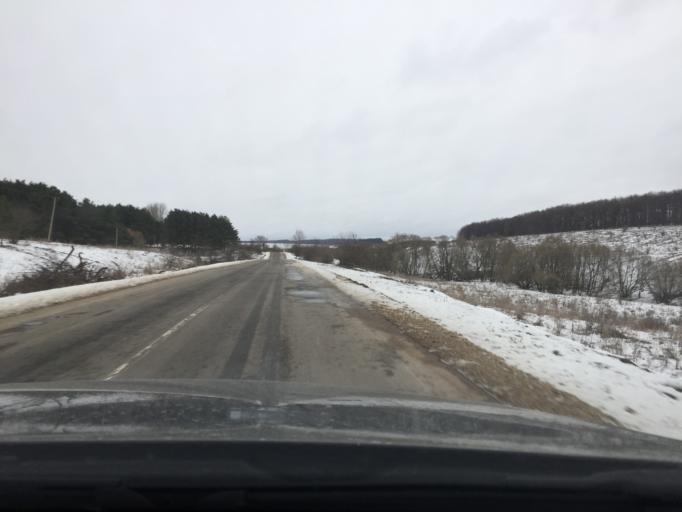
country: RU
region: Tula
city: Shchekino
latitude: 53.8274
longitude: 37.5594
